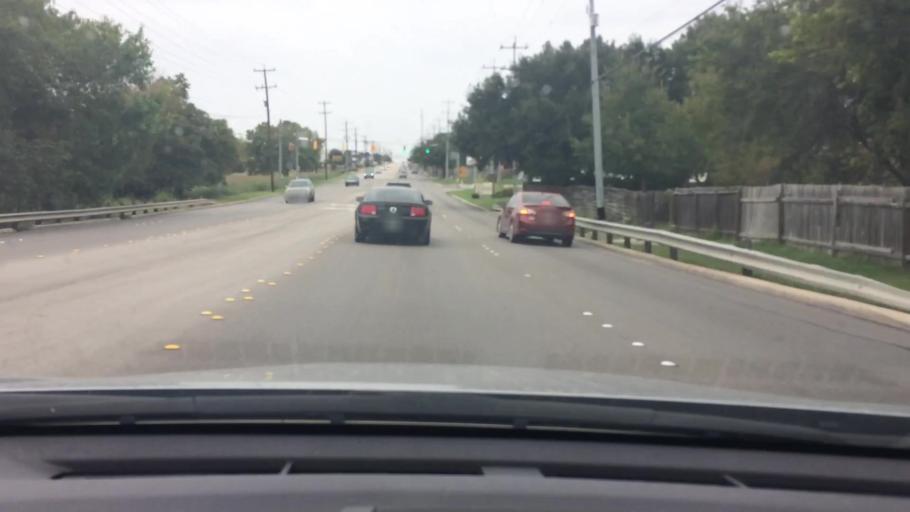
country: US
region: Texas
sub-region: Bexar County
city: Live Oak
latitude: 29.5391
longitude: -98.3373
